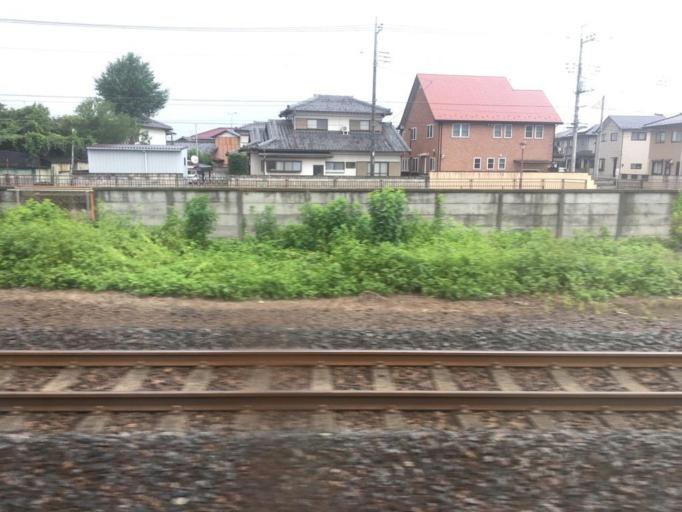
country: JP
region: Gunma
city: Sakai-nakajima
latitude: 36.2769
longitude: 139.2584
